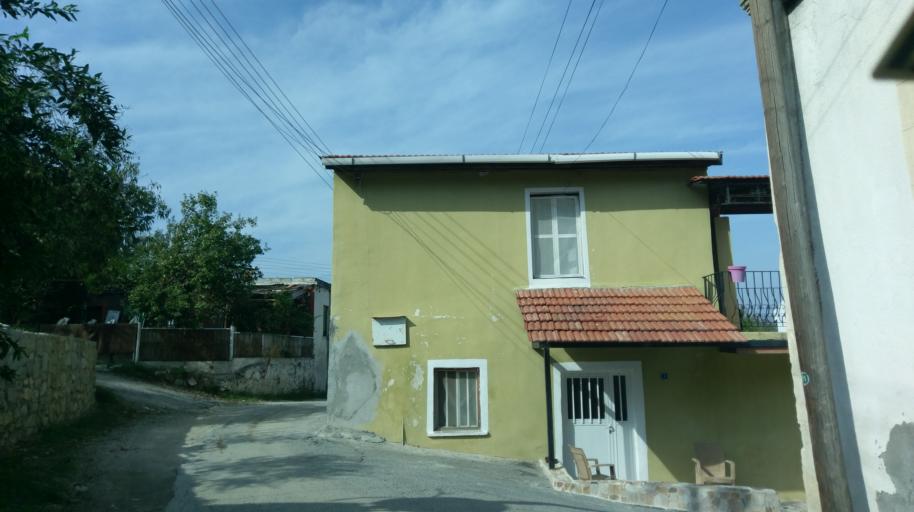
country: CY
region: Keryneia
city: Lapithos
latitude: 35.3258
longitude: 33.2086
